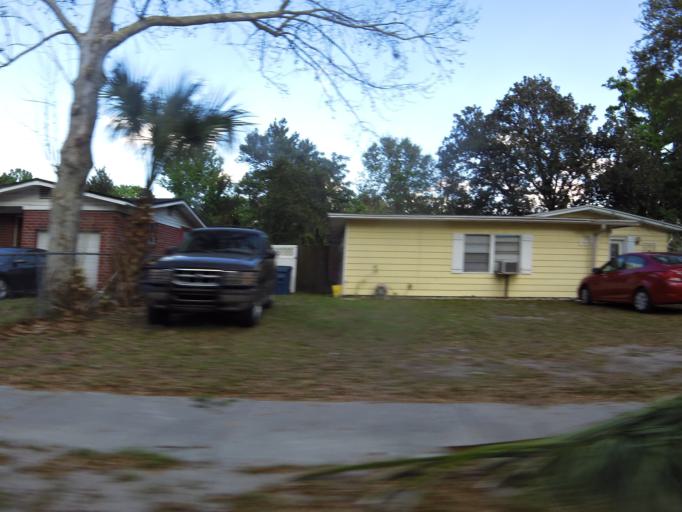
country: US
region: Florida
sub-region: Duval County
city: Jacksonville
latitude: 30.3411
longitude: -81.5973
